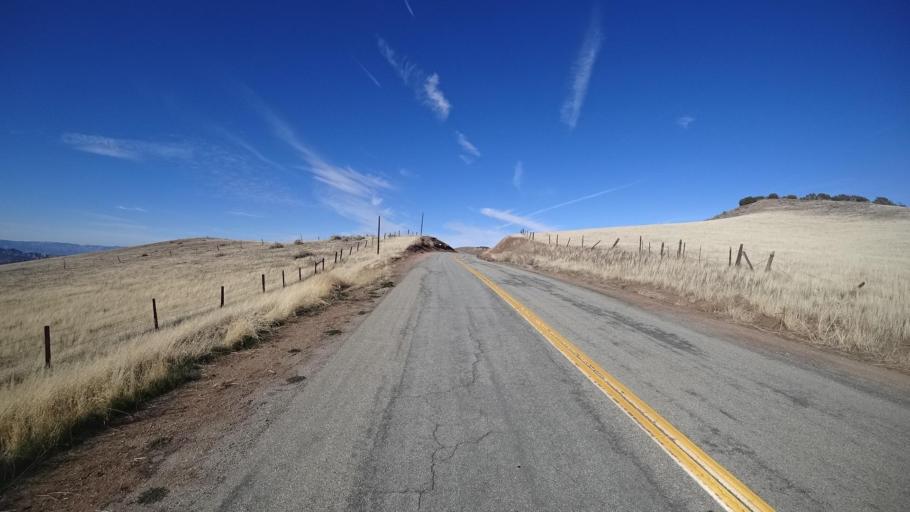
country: US
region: California
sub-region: Kern County
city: Maricopa
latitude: 34.8872
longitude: -119.3554
